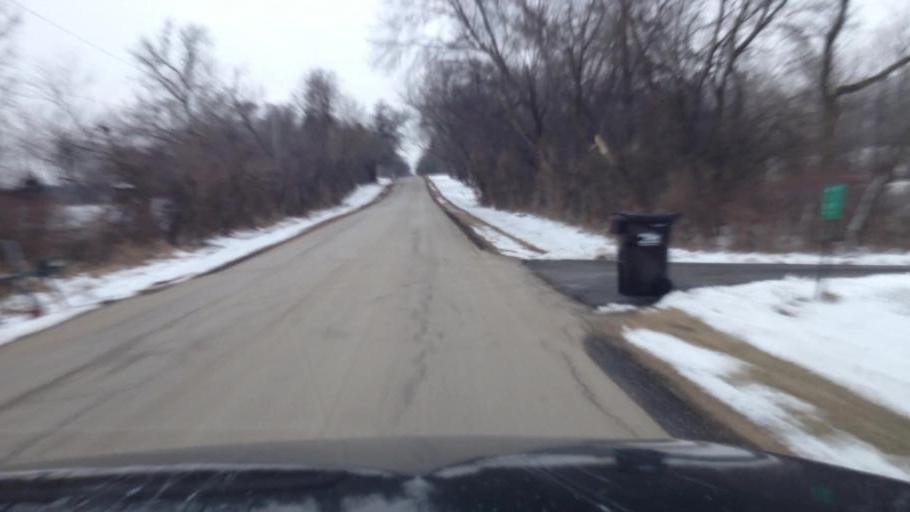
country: US
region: Illinois
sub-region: McHenry County
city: Woodstock
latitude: 42.2694
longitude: -88.4721
